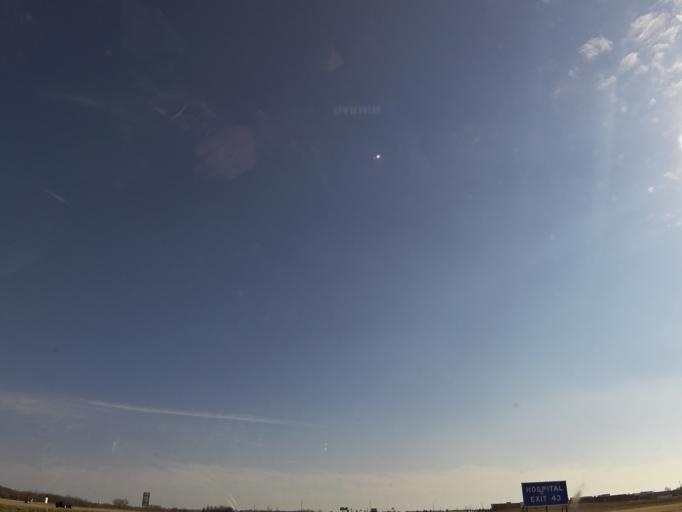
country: US
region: Minnesota
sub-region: Steele County
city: Owatonna
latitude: 44.1193
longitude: -93.2470
